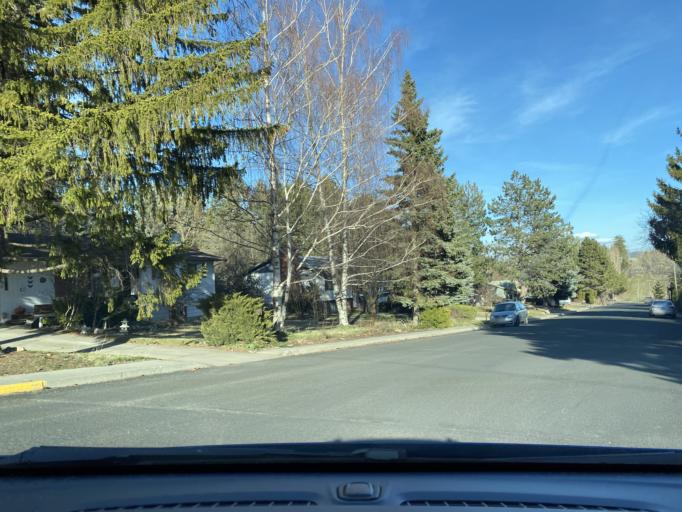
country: US
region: Idaho
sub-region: Latah County
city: Moscow
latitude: 46.7447
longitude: -116.9855
